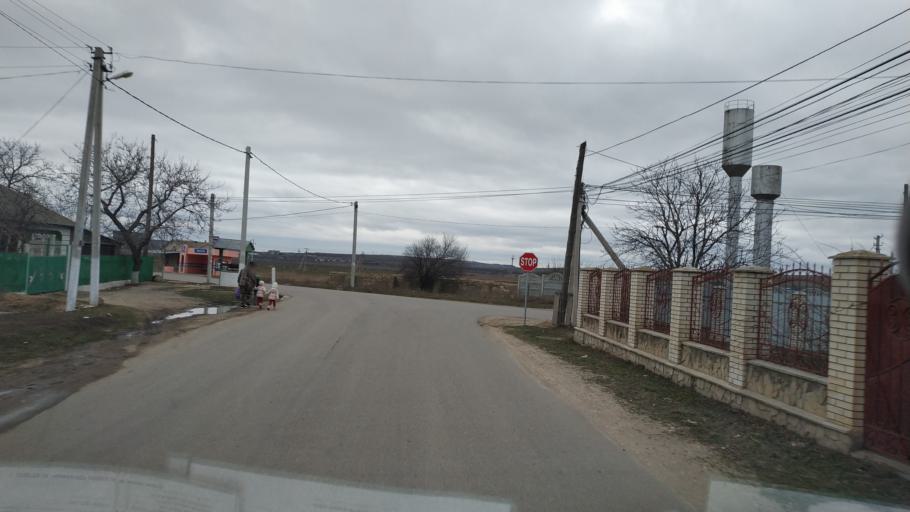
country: MD
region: Causeni
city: Causeni
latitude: 46.6671
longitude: 29.4828
